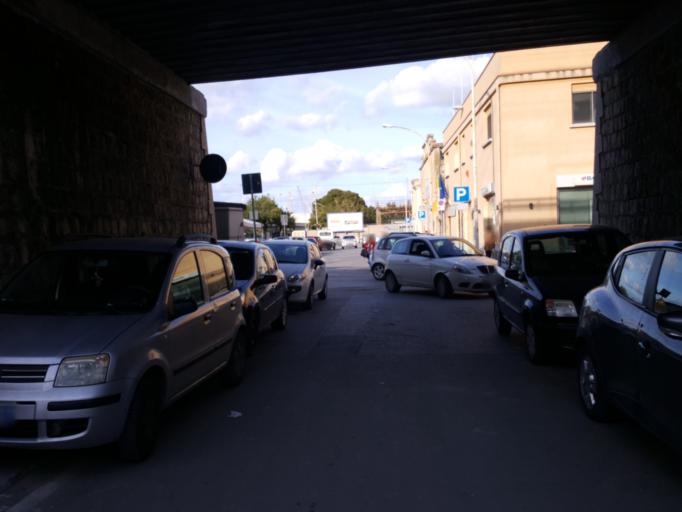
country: IT
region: Sicily
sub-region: Palermo
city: Termini Imerese
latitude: 37.9834
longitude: 13.7010
